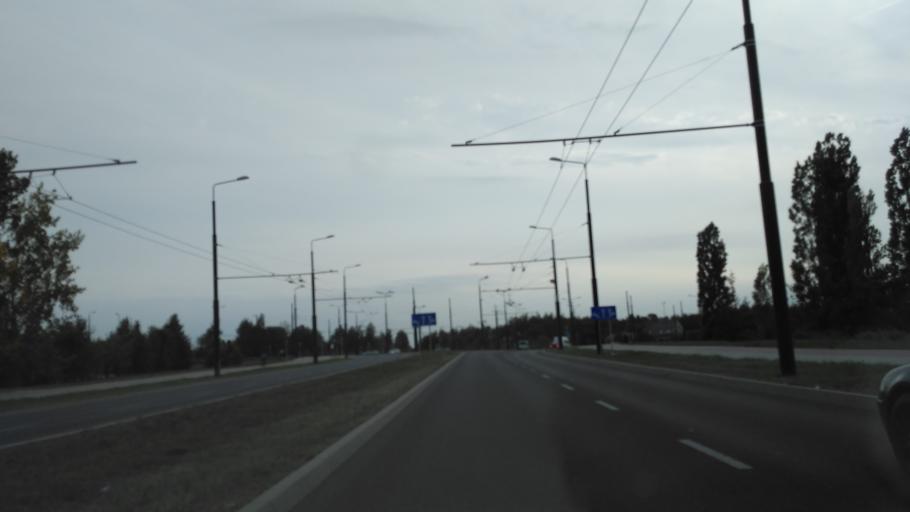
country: PL
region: Lublin Voivodeship
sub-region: Powiat lubelski
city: Jakubowice Murowane
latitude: 51.2247
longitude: 22.6153
